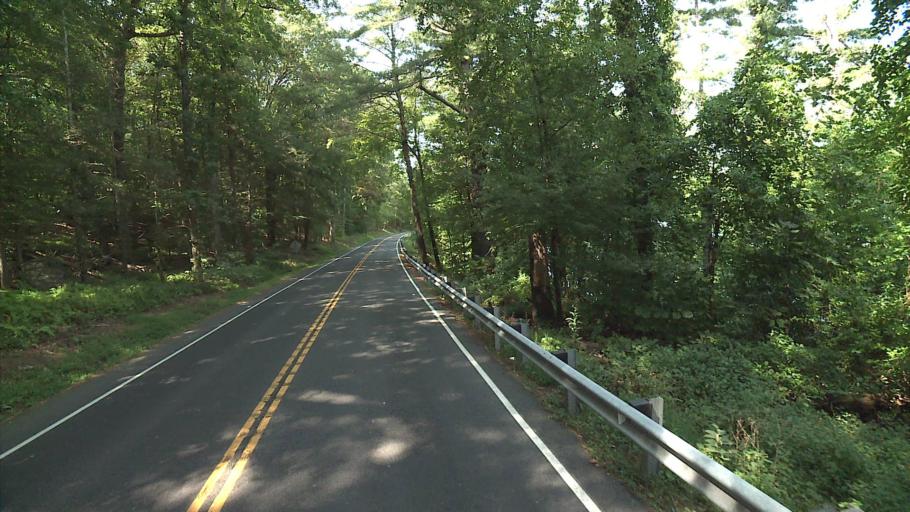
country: US
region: Connecticut
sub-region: Fairfield County
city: Southport
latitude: 41.2180
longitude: -73.2963
